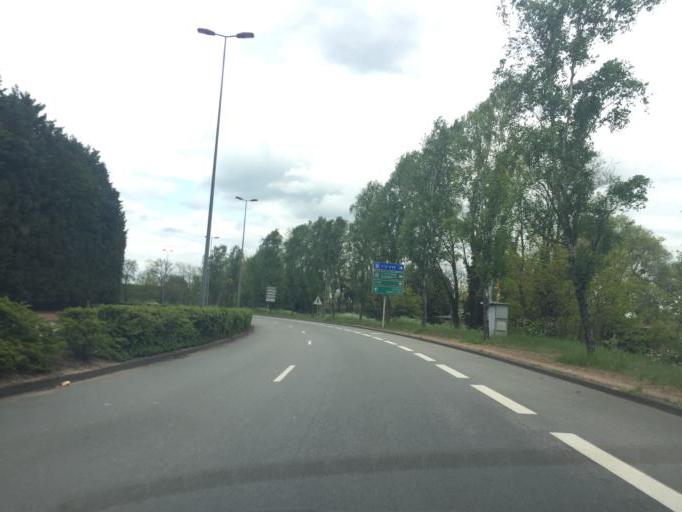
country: FR
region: Rhone-Alpes
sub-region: Departement de la Loire
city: Roanne
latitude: 46.0526
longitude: 4.0760
